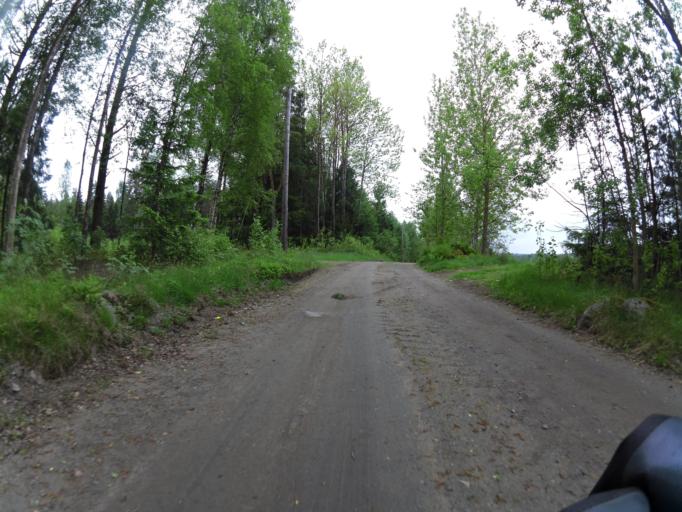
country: NO
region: Ostfold
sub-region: Rygge
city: Ryggebyen
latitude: 59.3632
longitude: 10.7158
